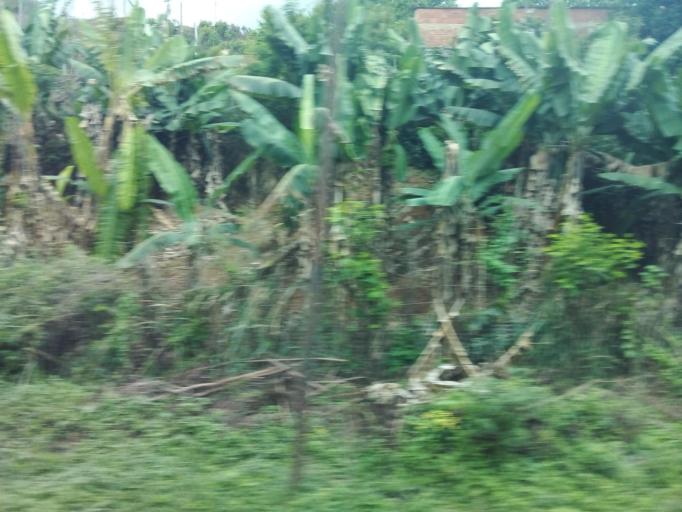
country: BR
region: Minas Gerais
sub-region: Coronel Fabriciano
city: Coronel Fabriciano
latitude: -19.5258
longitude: -42.6613
